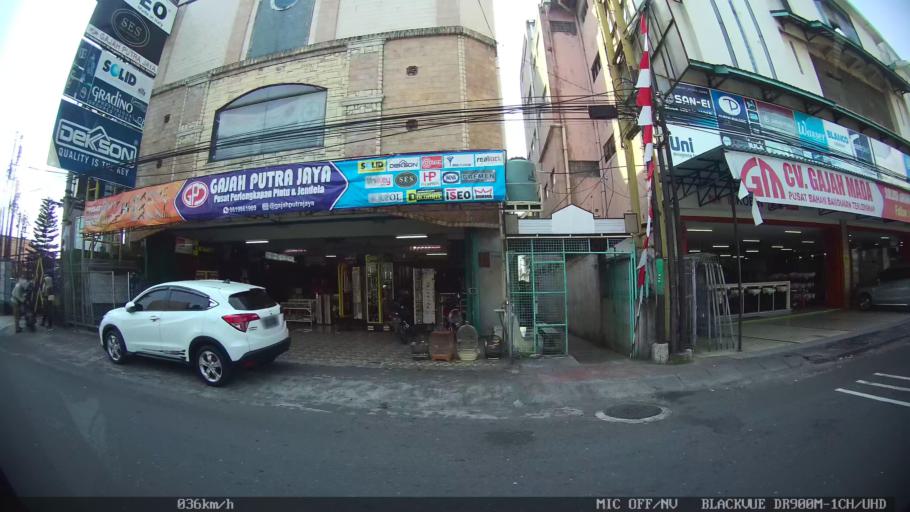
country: ID
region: Daerah Istimewa Yogyakarta
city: Yogyakarta
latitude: -7.7905
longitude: 110.3623
